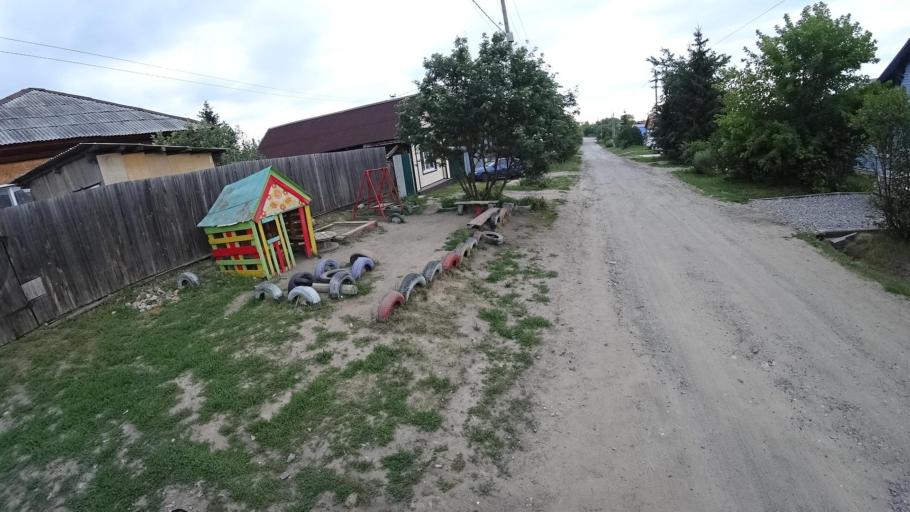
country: RU
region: Sverdlovsk
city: Kamyshlov
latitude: 56.8509
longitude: 62.6764
